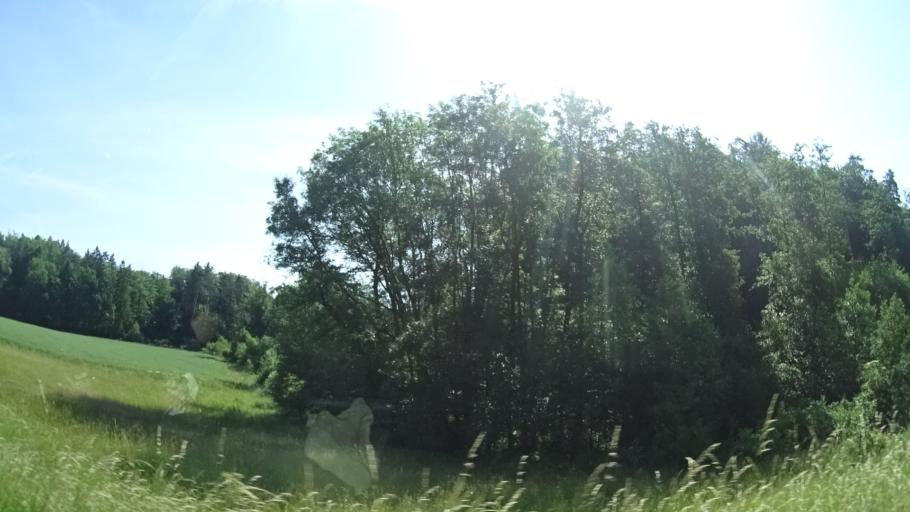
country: DE
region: Hesse
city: Beuern
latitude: 50.6487
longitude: 8.8313
